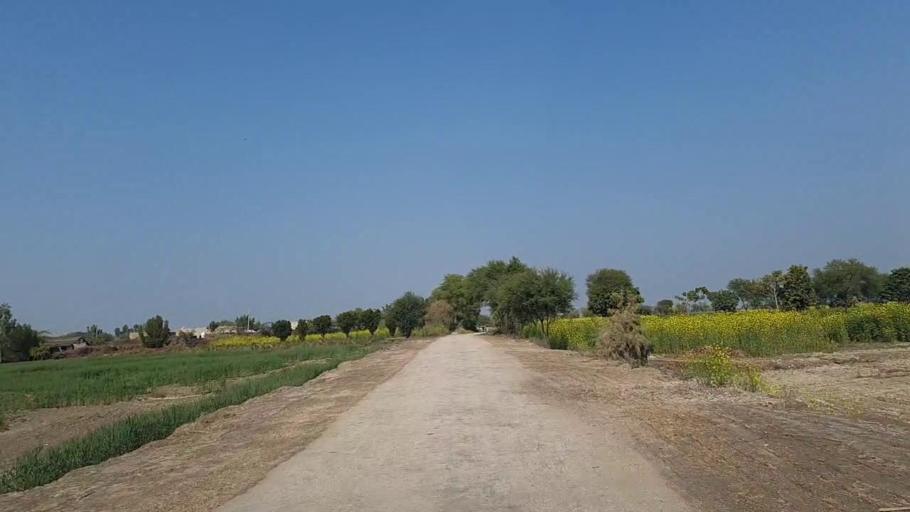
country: PK
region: Sindh
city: Nawabshah
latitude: 26.2898
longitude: 68.5138
